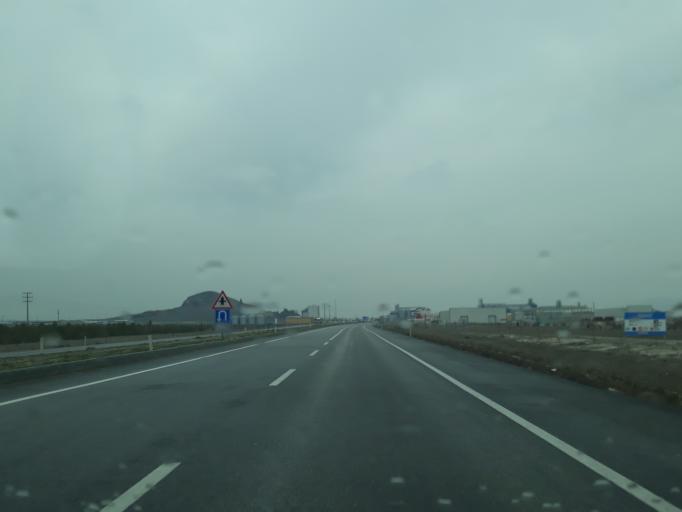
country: TR
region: Konya
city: Karapinar
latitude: 37.7133
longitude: 33.5978
